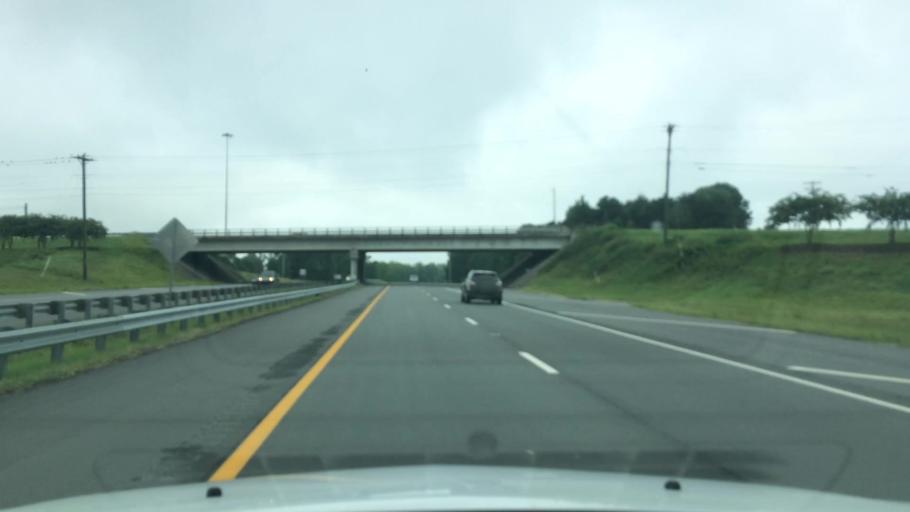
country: US
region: North Carolina
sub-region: Forsyth County
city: Lewisville
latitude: 36.0768
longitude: -80.3874
